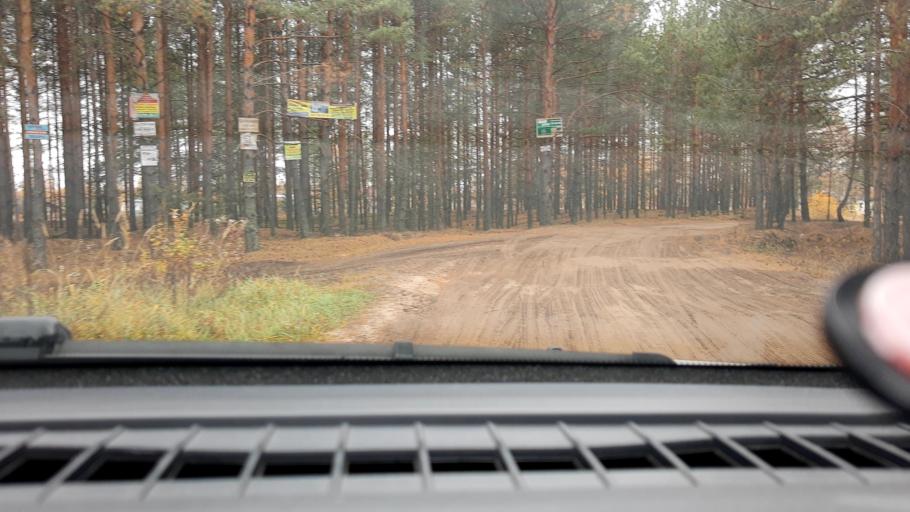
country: RU
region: Nizjnij Novgorod
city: Lukino
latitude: 56.3849
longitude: 43.6479
